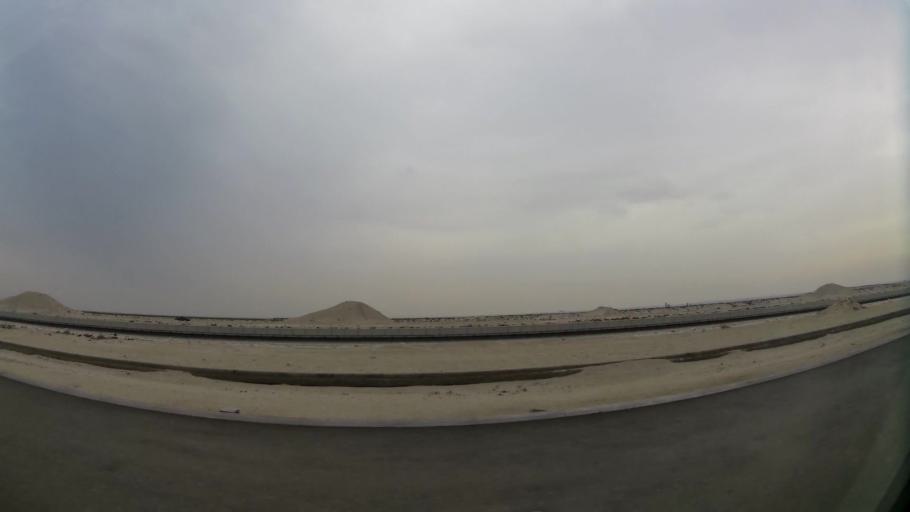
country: BH
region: Central Governorate
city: Dar Kulayb
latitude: 25.8656
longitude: 50.6044
